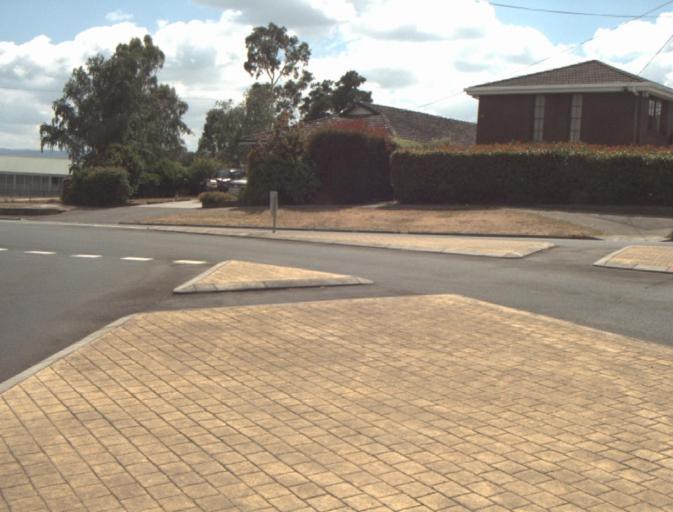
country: AU
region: Tasmania
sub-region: Launceston
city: Newstead
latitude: -41.4638
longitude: 147.1734
